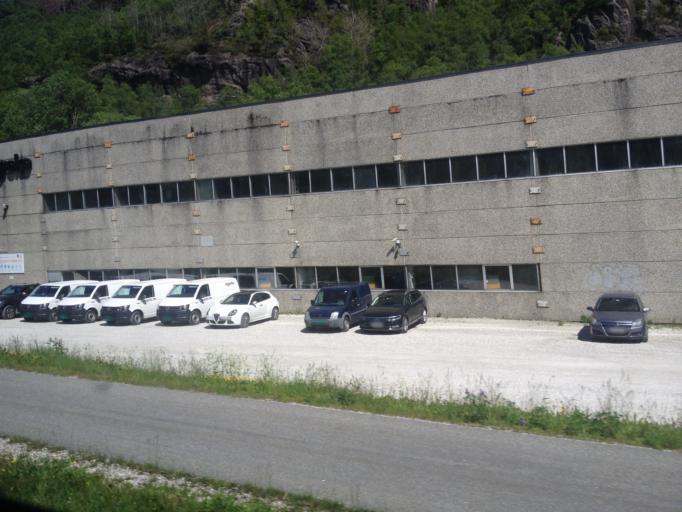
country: NO
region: Rogaland
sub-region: Bjerkreim
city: Vikesa
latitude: 58.5233
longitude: 6.0980
